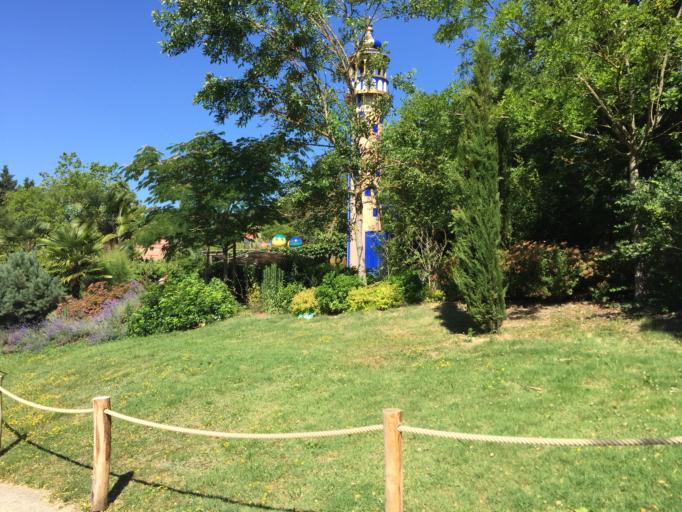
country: FR
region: Auvergne
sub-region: Departement de l'Allier
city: Dompierre-sur-Besbre
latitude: 46.5075
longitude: 3.6326
